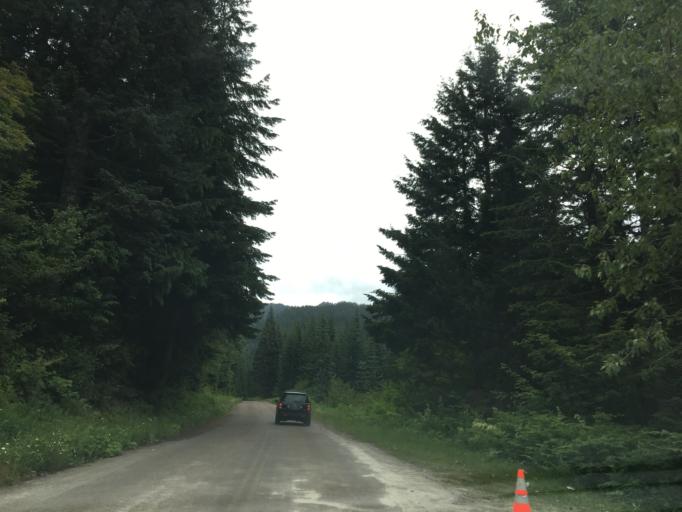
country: US
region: Washington
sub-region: Chelan County
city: Leavenworth
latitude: 47.7507
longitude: -121.1200
